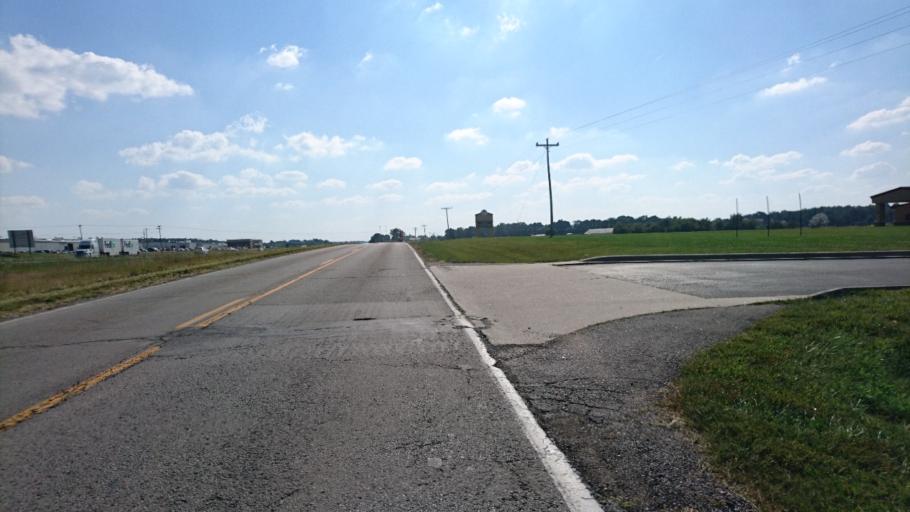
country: US
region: Missouri
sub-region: Laclede County
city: Lebanon
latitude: 37.6432
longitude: -92.6728
